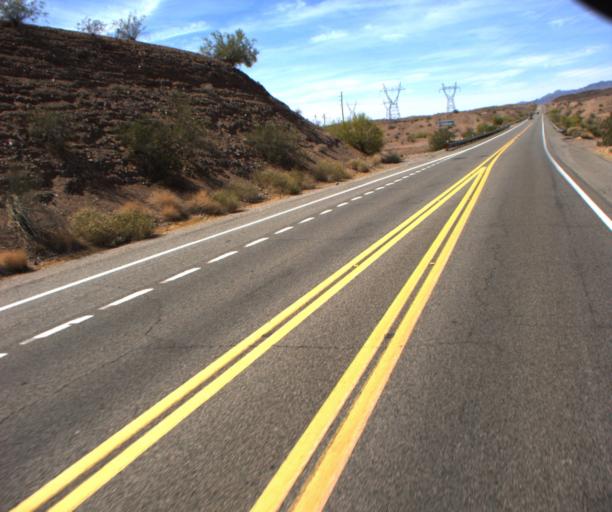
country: US
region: Arizona
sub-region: La Paz County
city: Cienega Springs
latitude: 34.3617
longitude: -114.1582
